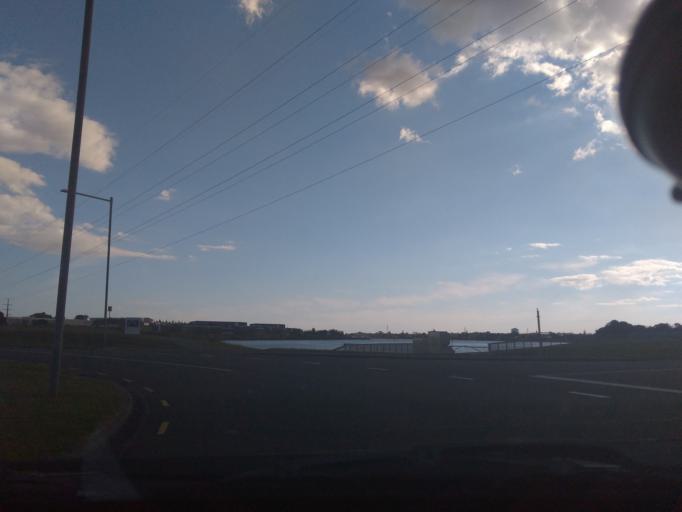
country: NZ
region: Auckland
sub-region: Auckland
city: Tamaki
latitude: -36.9313
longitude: 174.8712
